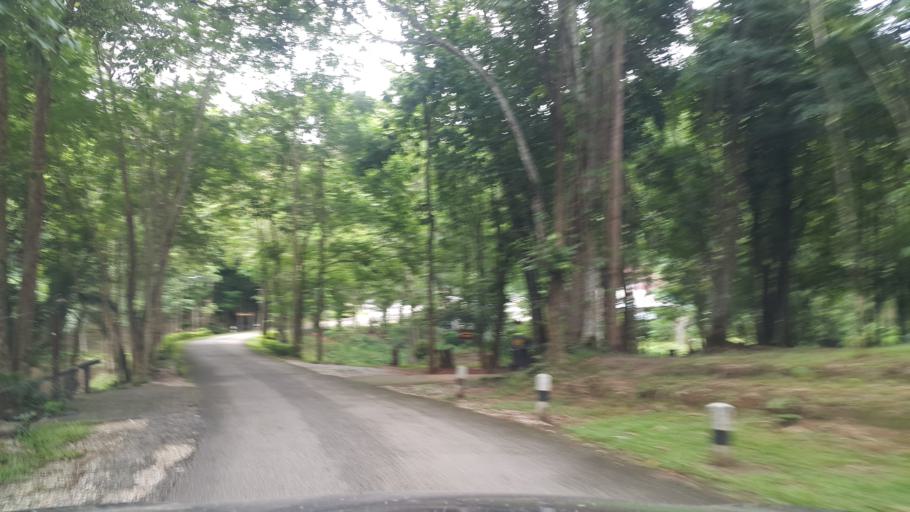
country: TH
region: Phitsanulok
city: Chat Trakan
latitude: 17.3006
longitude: 100.6788
